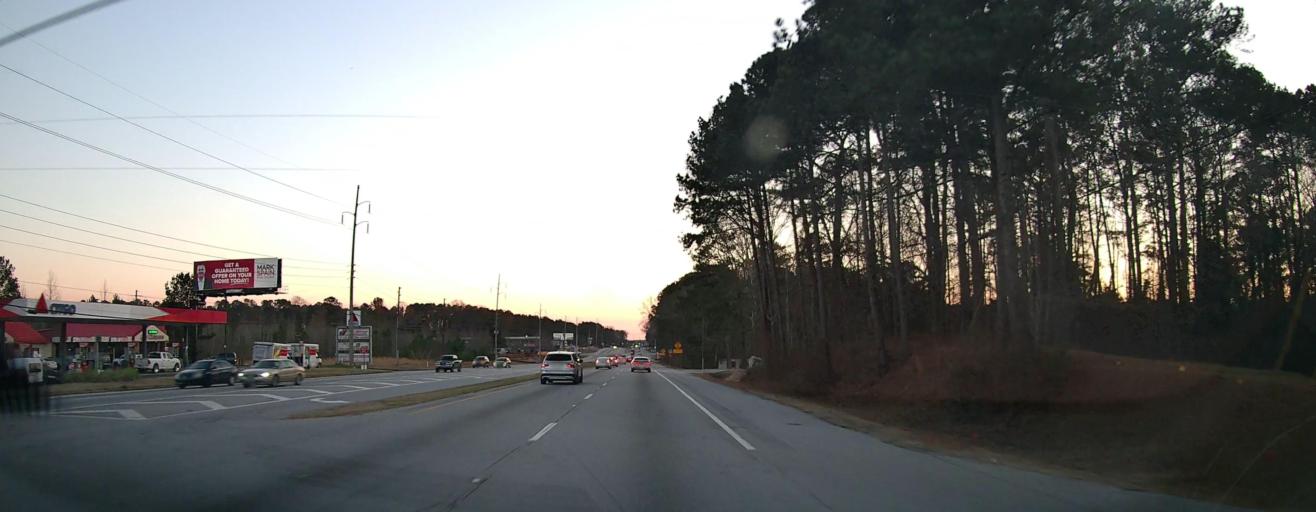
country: US
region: Georgia
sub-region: Clayton County
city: Riverdale
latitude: 33.5378
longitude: -84.4180
